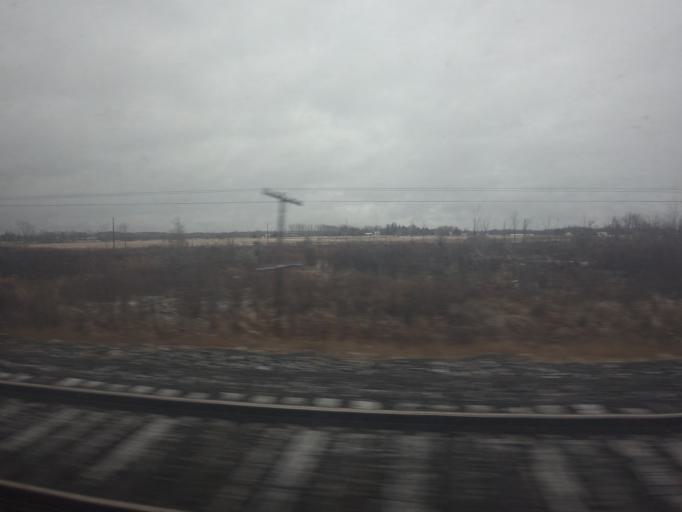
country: CA
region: Ontario
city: Gananoque
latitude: 44.3797
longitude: -76.0749
